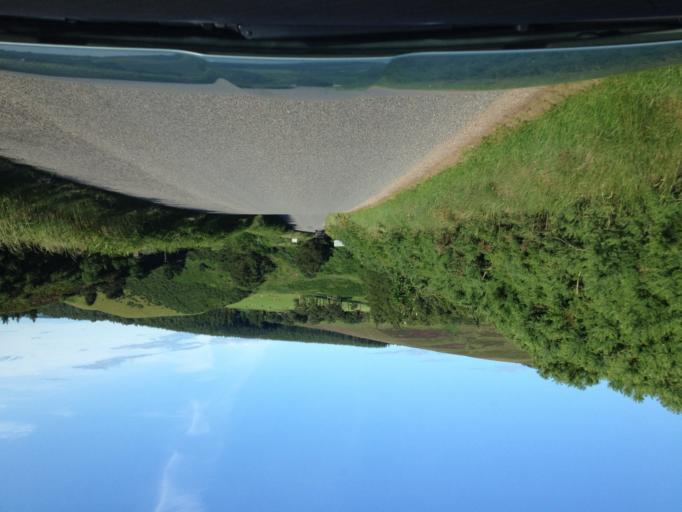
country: GB
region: Scotland
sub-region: Aberdeenshire
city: Laurencekirk
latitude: 56.8959
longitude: -2.5543
